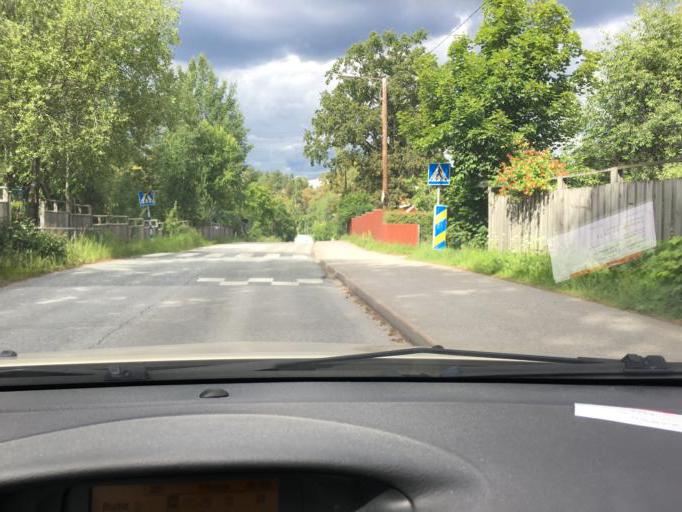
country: SE
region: Stockholm
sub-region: Nacka Kommun
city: Fisksatra
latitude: 59.3070
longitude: 18.2578
